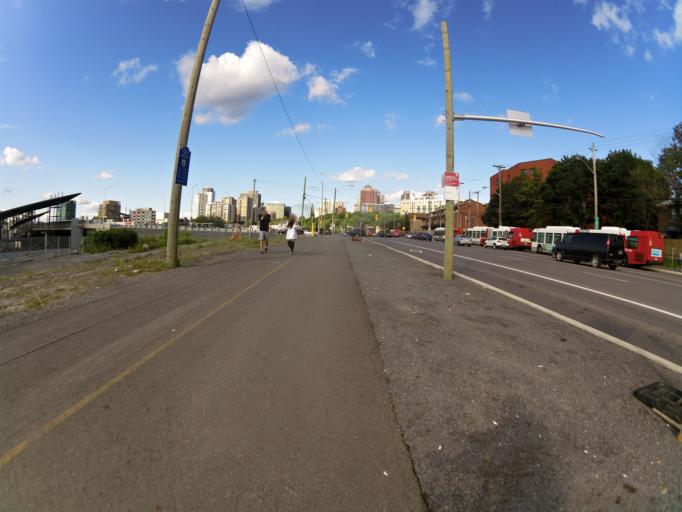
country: CA
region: Ontario
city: Ottawa
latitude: 45.4126
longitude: -75.7137
